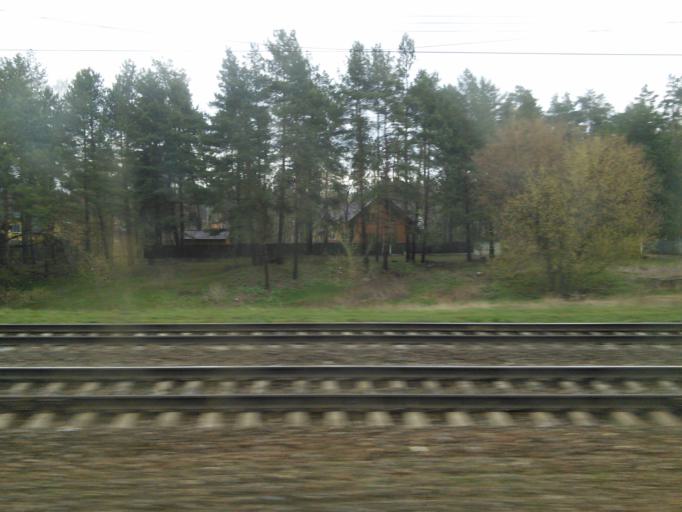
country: RU
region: Moskovskaya
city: Kratovo
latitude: 55.5853
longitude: 38.1769
